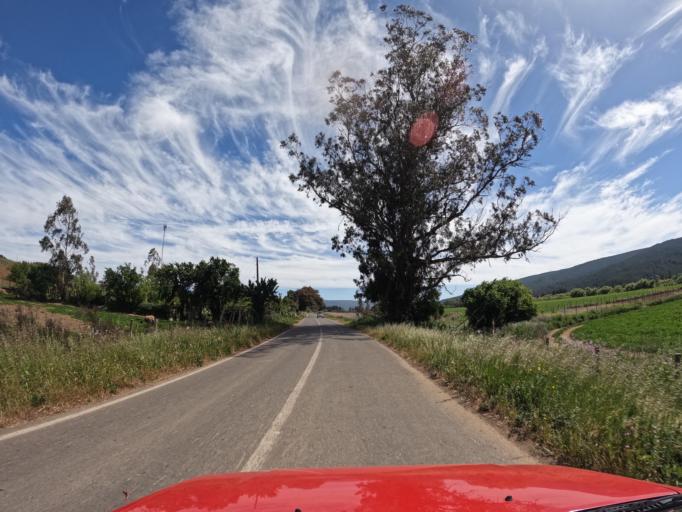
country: CL
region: Maule
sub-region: Provincia de Talca
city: Constitucion
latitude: -35.0069
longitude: -72.0319
